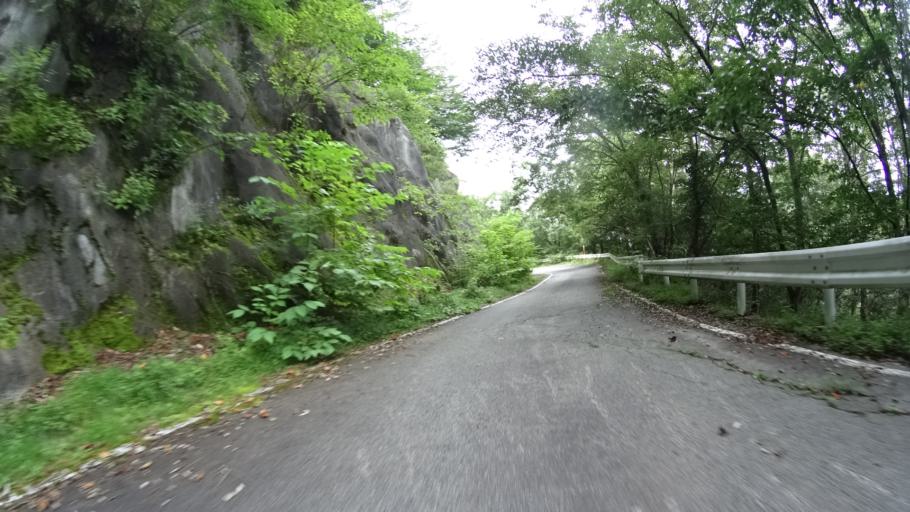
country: JP
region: Yamanashi
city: Kofu-shi
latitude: 35.8098
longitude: 138.5521
